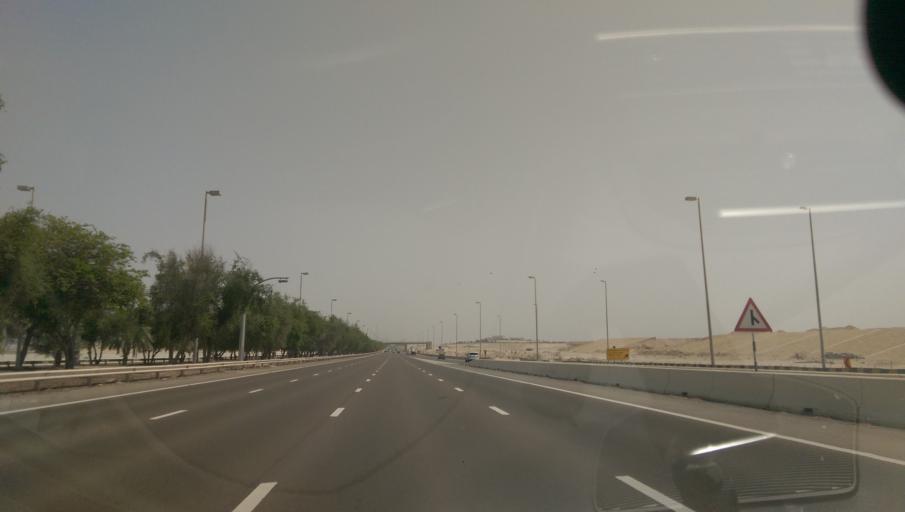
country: AE
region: Abu Dhabi
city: Abu Dhabi
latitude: 24.4236
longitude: 54.6777
